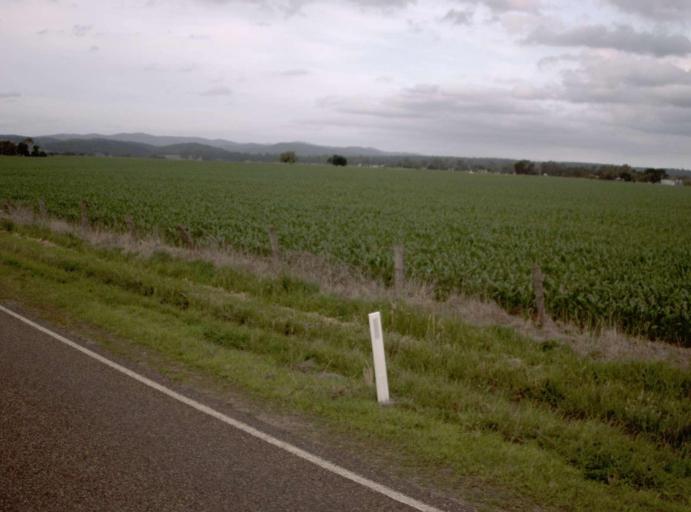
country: AU
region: Victoria
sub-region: Wellington
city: Sale
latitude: -37.8463
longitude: 147.0549
